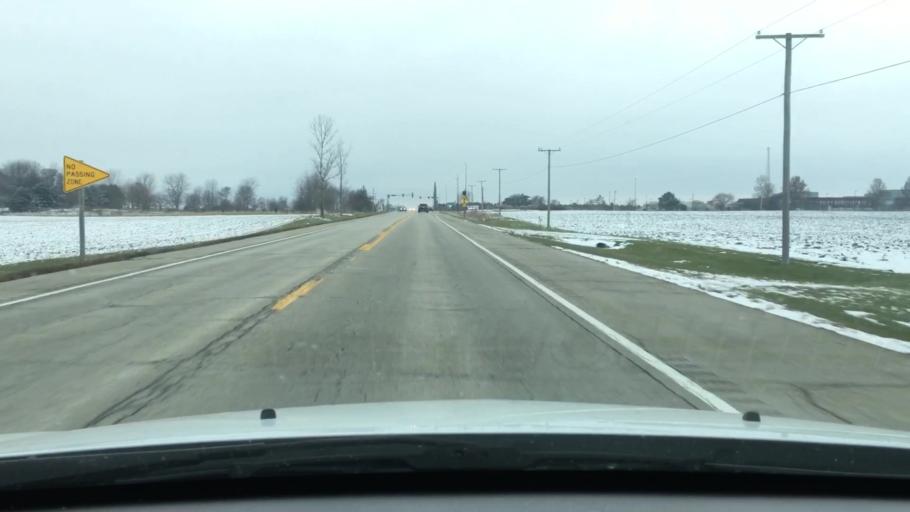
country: US
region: Illinois
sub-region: DeKalb County
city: Malta
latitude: 41.9357
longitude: -88.8727
